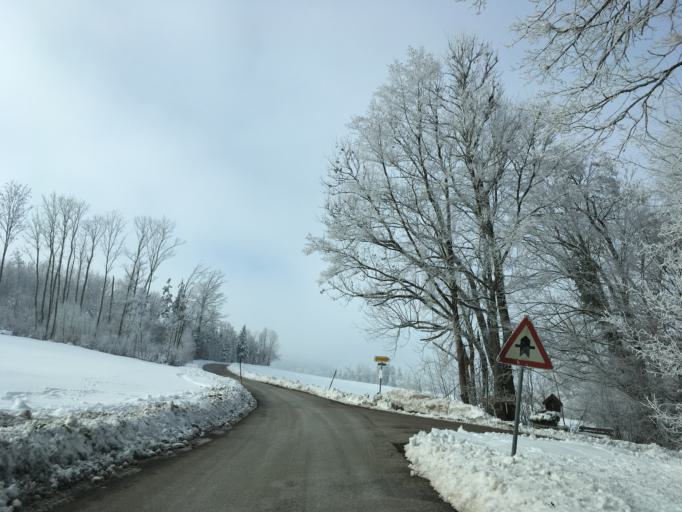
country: DE
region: Bavaria
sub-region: Upper Bavaria
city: Frasdorf
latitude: 47.8515
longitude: 12.2800
